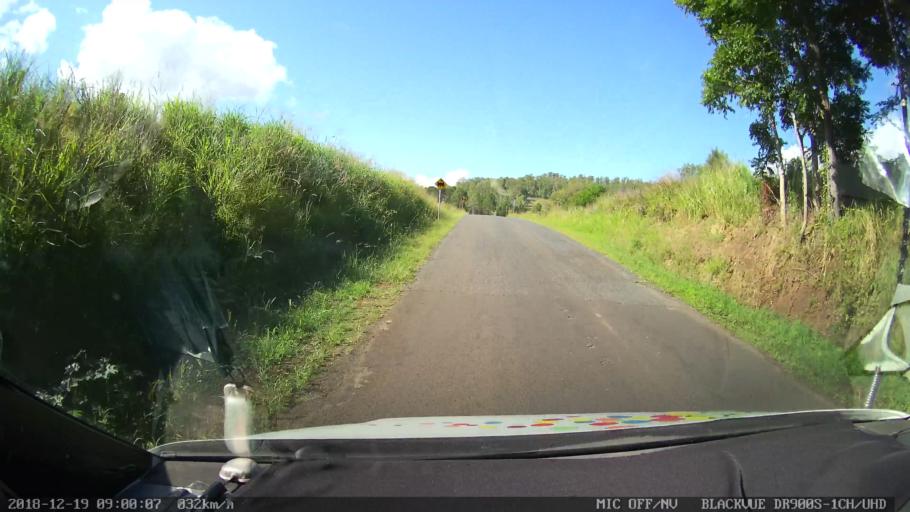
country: AU
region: New South Wales
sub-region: Kyogle
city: Kyogle
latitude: -28.4298
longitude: 152.9578
